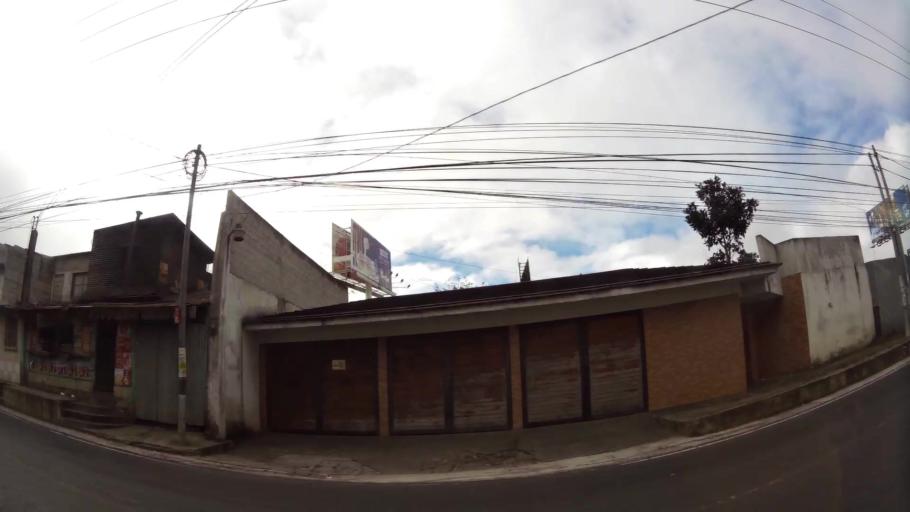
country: GT
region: Guatemala
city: Santa Catarina Pinula
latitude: 14.5651
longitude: -90.4655
